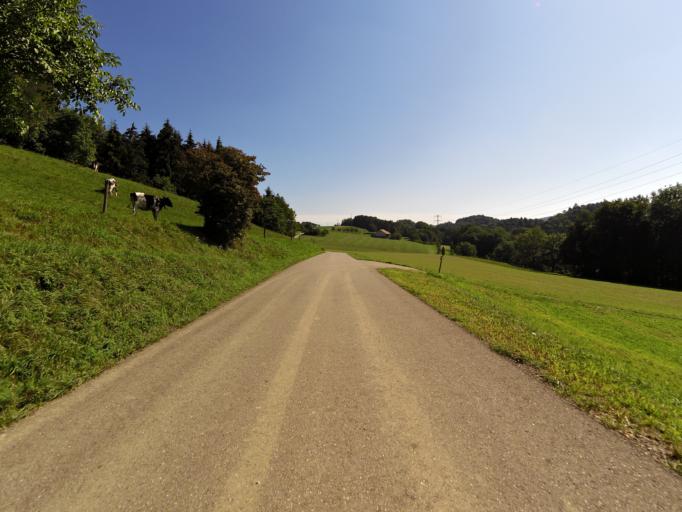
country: CH
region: Thurgau
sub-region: Weinfelden District
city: Maerstetten-Dorf
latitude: 47.6013
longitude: 9.0655
